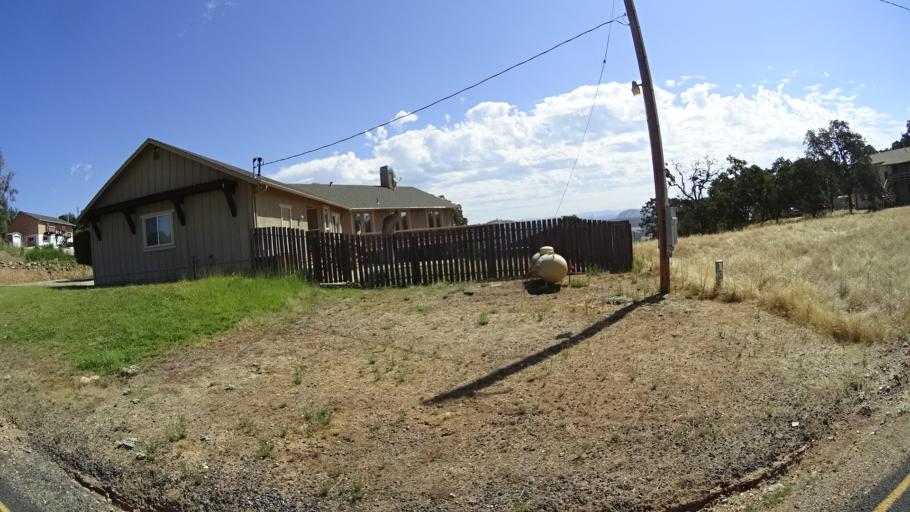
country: US
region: California
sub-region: Calaveras County
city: Copperopolis
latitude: 37.9265
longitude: -120.6317
